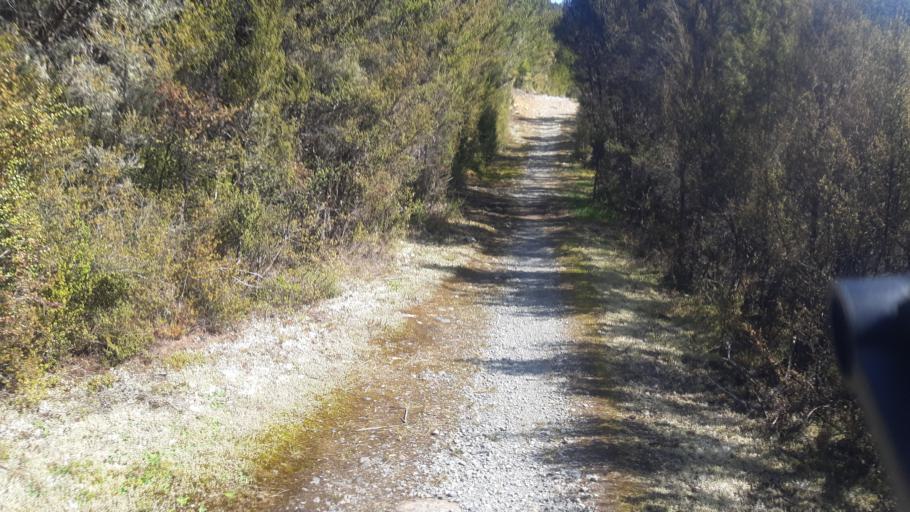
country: NZ
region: Tasman
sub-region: Tasman District
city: Wakefield
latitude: -41.7999
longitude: 172.8387
